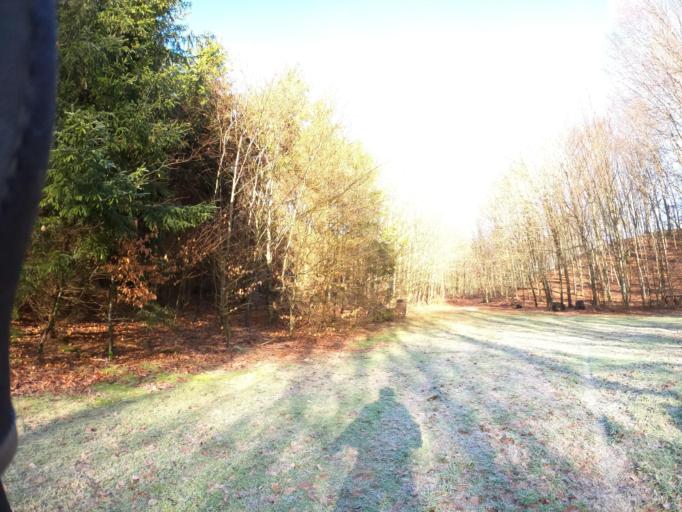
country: PL
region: West Pomeranian Voivodeship
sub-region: Powiat koszalinski
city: Polanow
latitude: 54.1143
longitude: 16.7212
